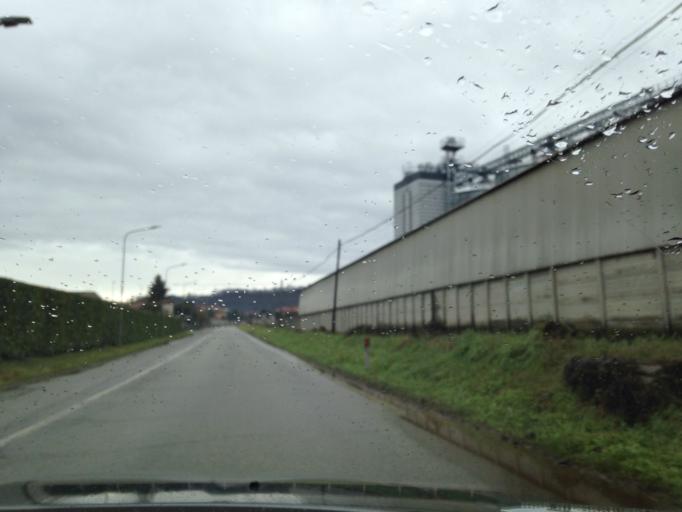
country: IT
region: Piedmont
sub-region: Provincia di Torino
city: Villareggia
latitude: 45.3043
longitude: 7.9782
